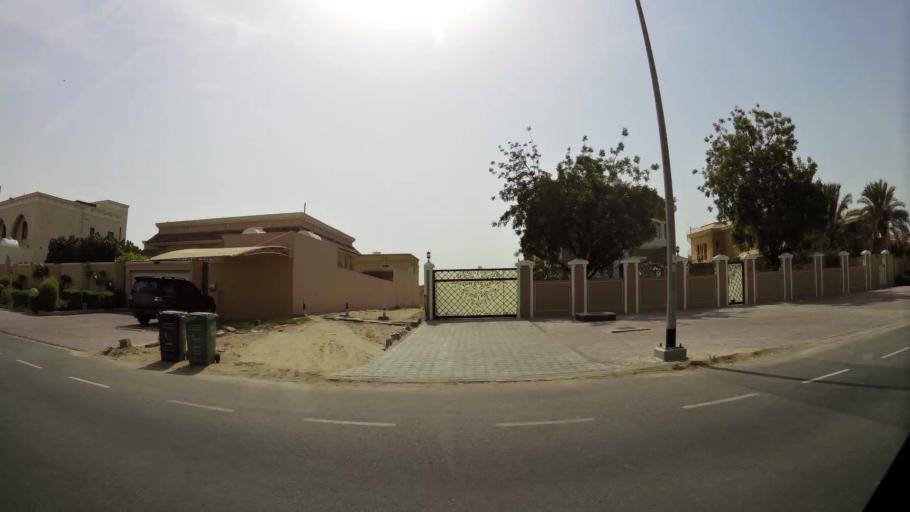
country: AE
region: Ash Shariqah
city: Sharjah
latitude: 25.2488
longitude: 55.4409
